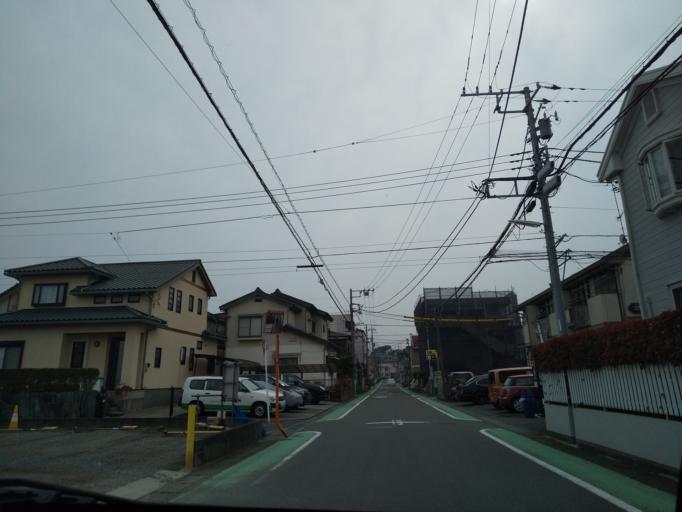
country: JP
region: Kanagawa
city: Minami-rinkan
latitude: 35.4684
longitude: 139.4259
